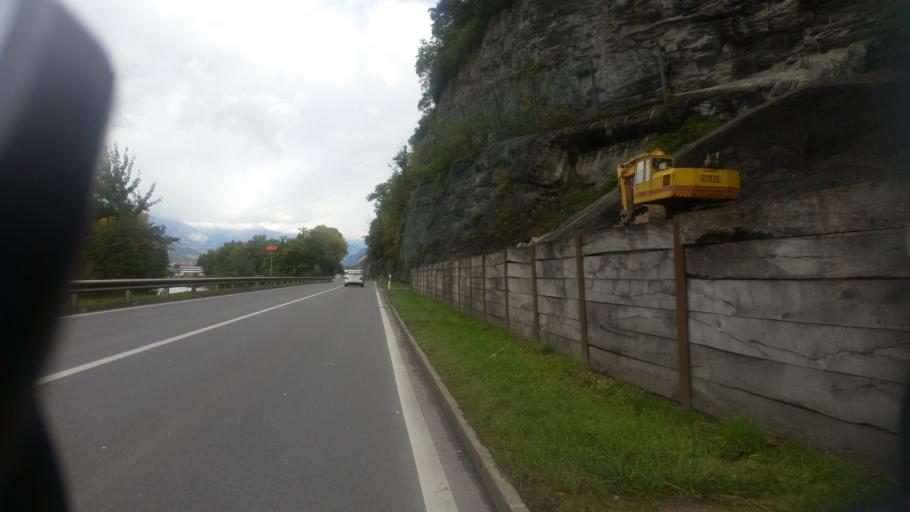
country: CH
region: Valais
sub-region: Sion District
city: Sitten
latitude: 46.2186
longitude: 7.3561
